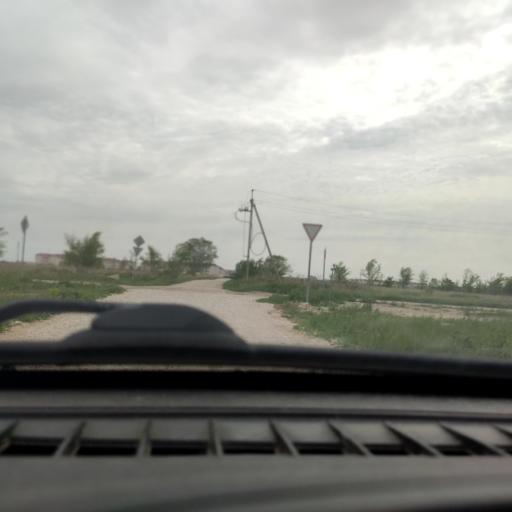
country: RU
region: Samara
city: Podstepki
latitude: 53.5284
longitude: 49.1689
